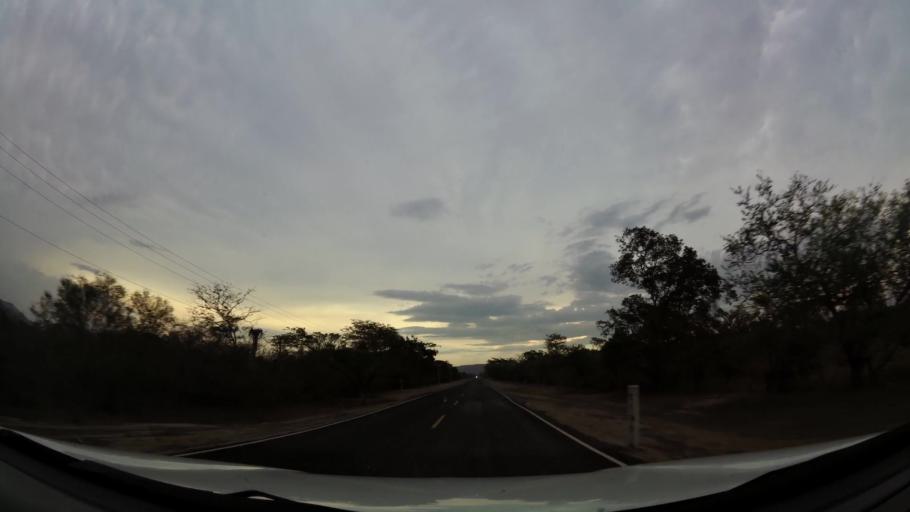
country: NI
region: Matagalpa
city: Ciudad Dario
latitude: 12.8749
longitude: -86.1921
